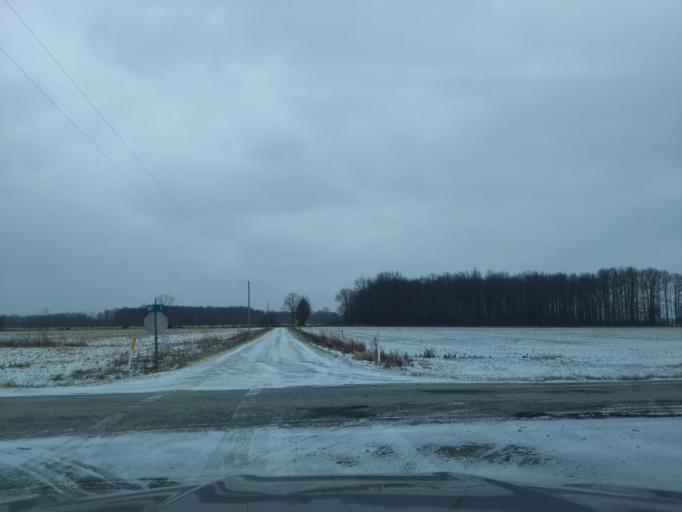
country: US
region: Indiana
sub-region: Decatur County
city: Westport
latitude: 39.2047
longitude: -85.4636
